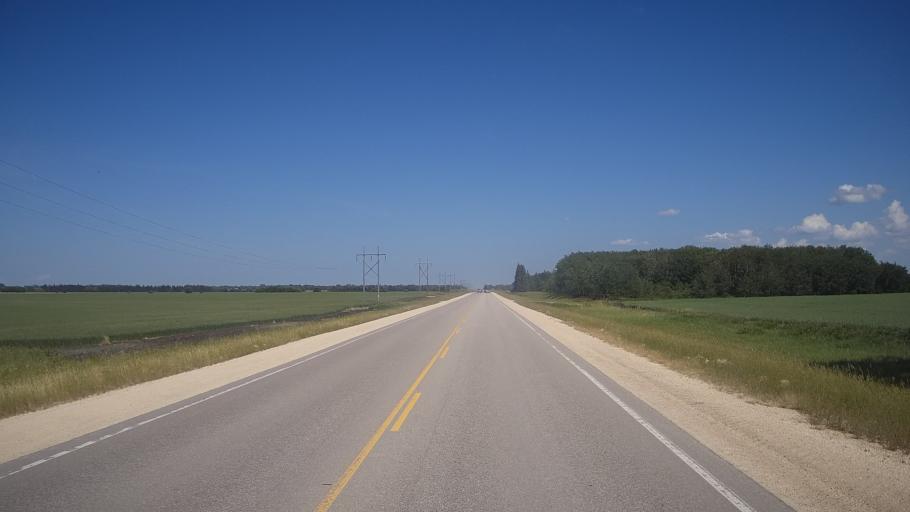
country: CA
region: Manitoba
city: Stonewall
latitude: 50.1227
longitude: -97.3658
